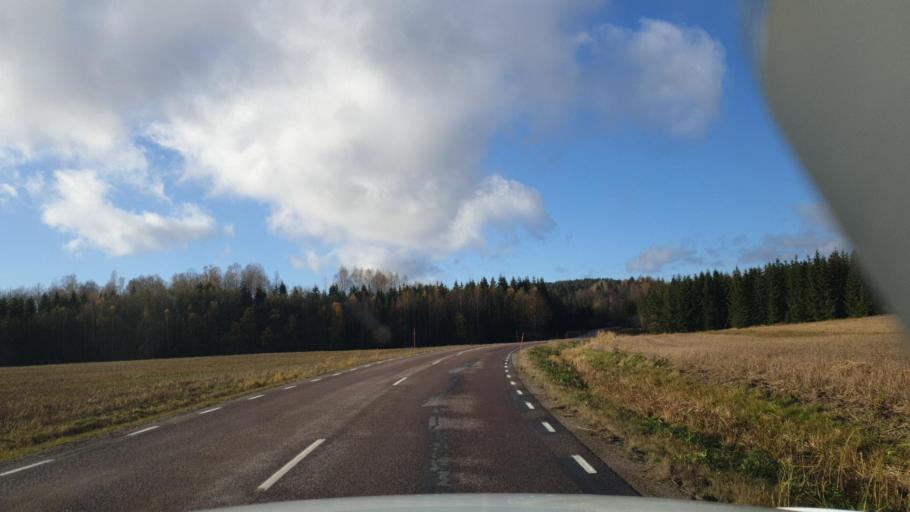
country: SE
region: Vaermland
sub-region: Grums Kommun
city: Slottsbron
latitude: 59.4442
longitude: 12.8721
